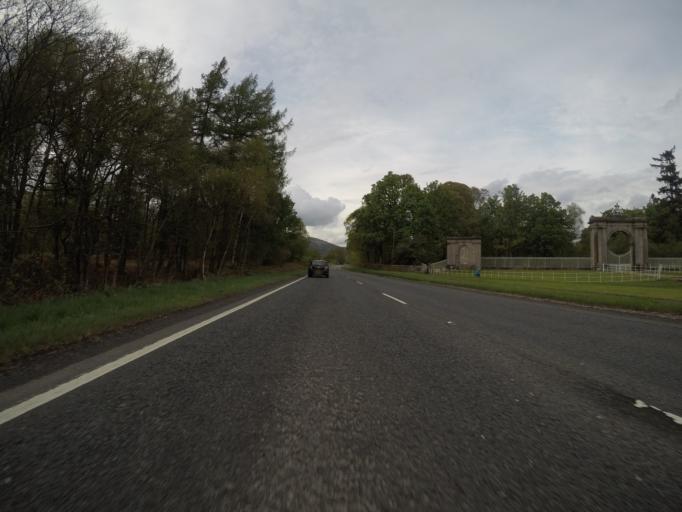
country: GB
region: Scotland
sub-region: West Dunbartonshire
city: Balloch
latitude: 56.0457
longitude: -4.6464
